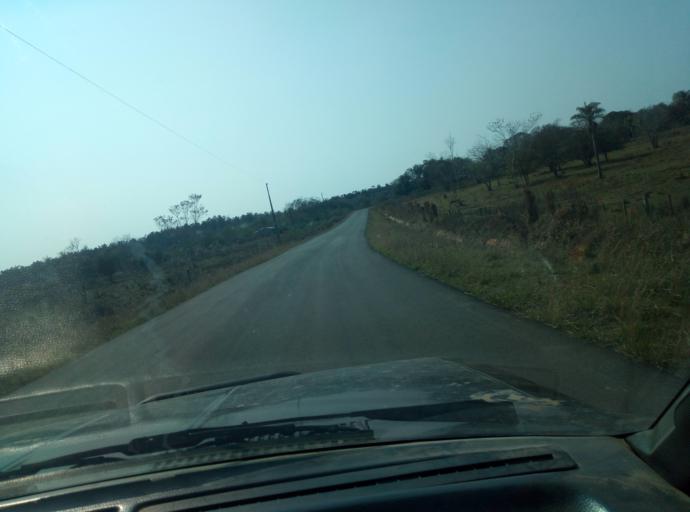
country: PY
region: Caaguazu
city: Carayao
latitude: -25.2633
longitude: -56.2836
